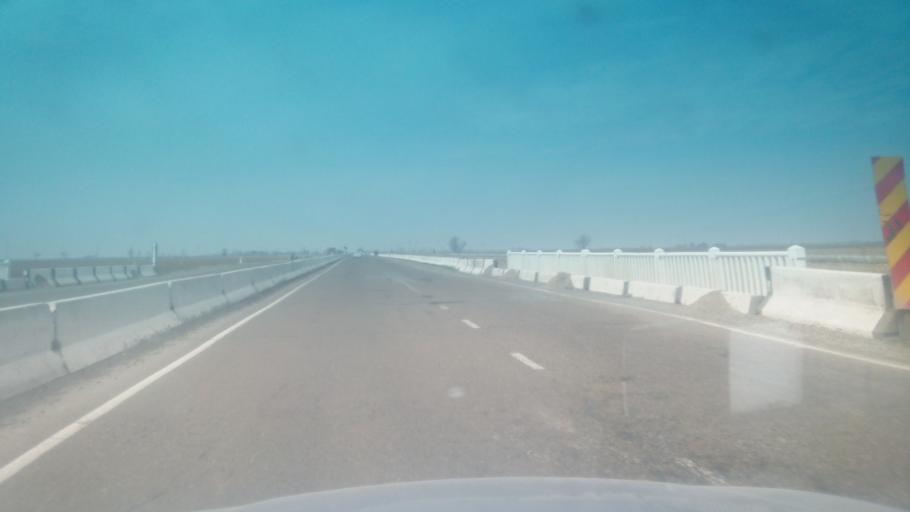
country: KZ
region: Ongtustik Qazaqstan
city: Myrzakent
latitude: 40.5179
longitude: 68.4745
